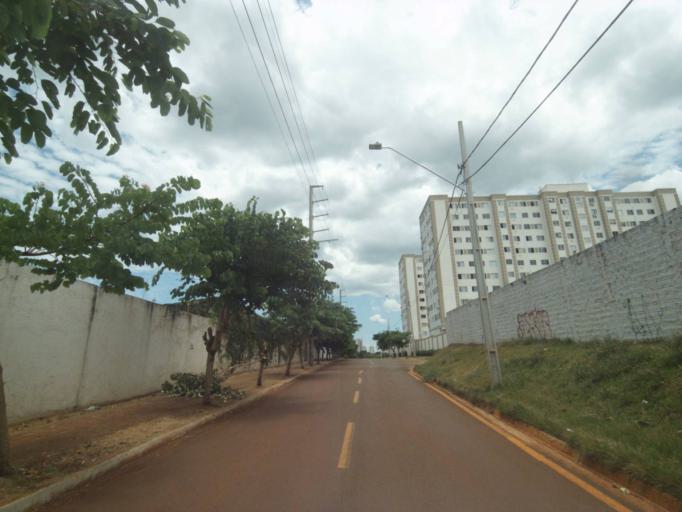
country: BR
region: Parana
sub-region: Londrina
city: Londrina
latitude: -23.3220
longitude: -51.1883
